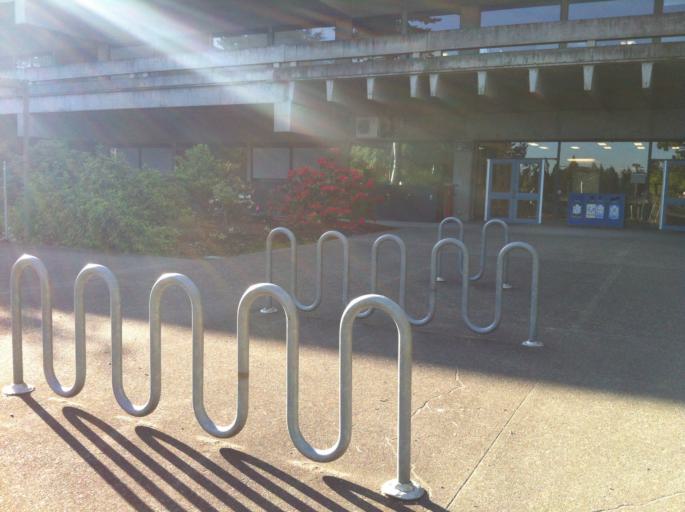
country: US
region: Oregon
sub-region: Washington County
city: Metzger
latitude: 45.4396
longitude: -122.7328
